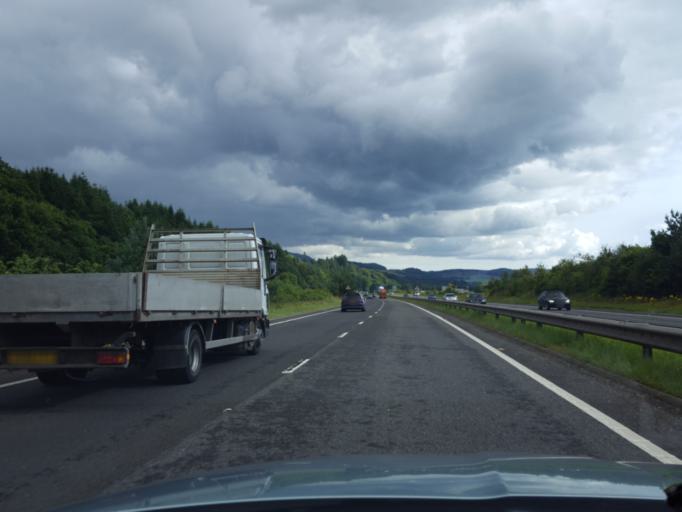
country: GB
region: Scotland
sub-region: Perth and Kinross
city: Pitlochry
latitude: 56.6496
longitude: -3.6657
